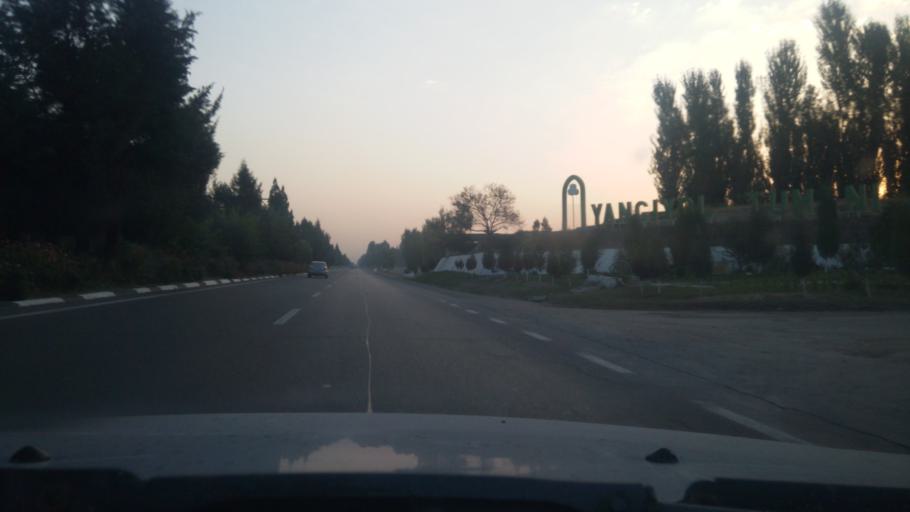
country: UZ
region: Toshkent
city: Amir Timur
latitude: 41.0549
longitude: 68.9018
